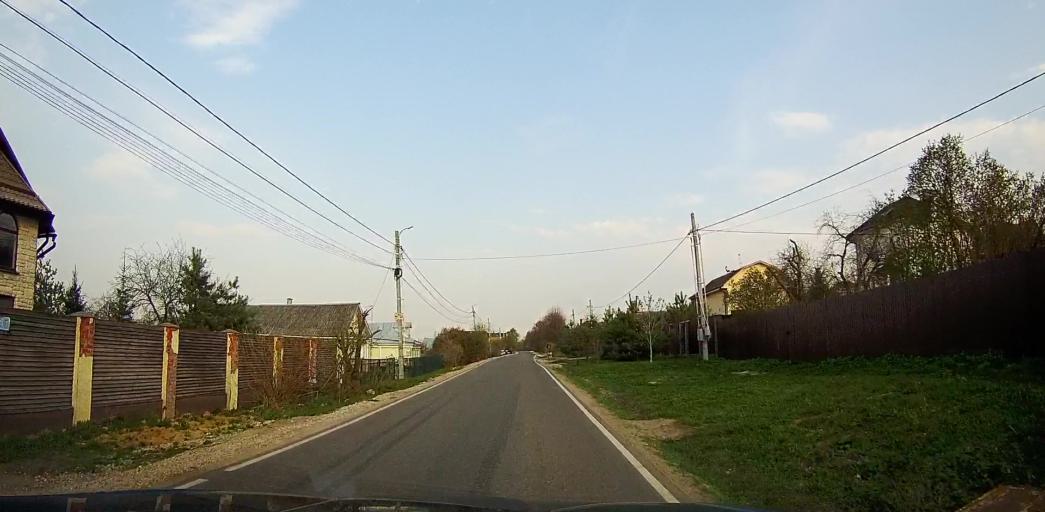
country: RU
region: Moskovskaya
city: Andreyevskoye
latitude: 55.5563
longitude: 37.9221
